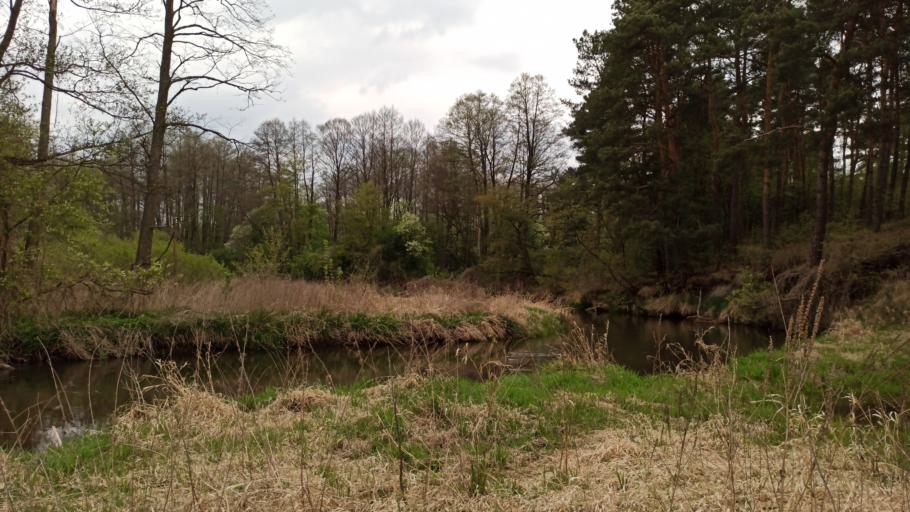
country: PL
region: Lodz Voivodeship
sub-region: Powiat skierniewicki
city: Kaweczyn Nowy
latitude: 51.9430
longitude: 20.2822
